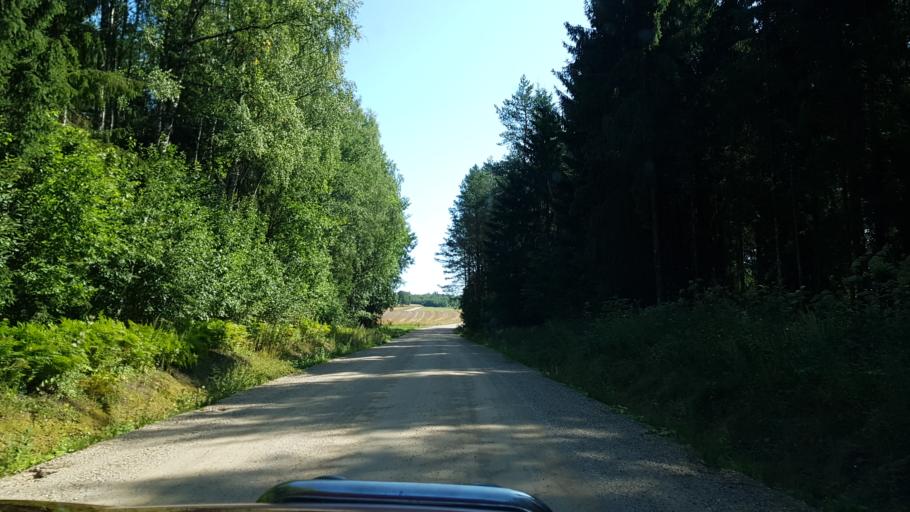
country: EE
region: Vorumaa
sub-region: Voru linn
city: Voru
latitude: 57.7362
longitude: 27.2389
